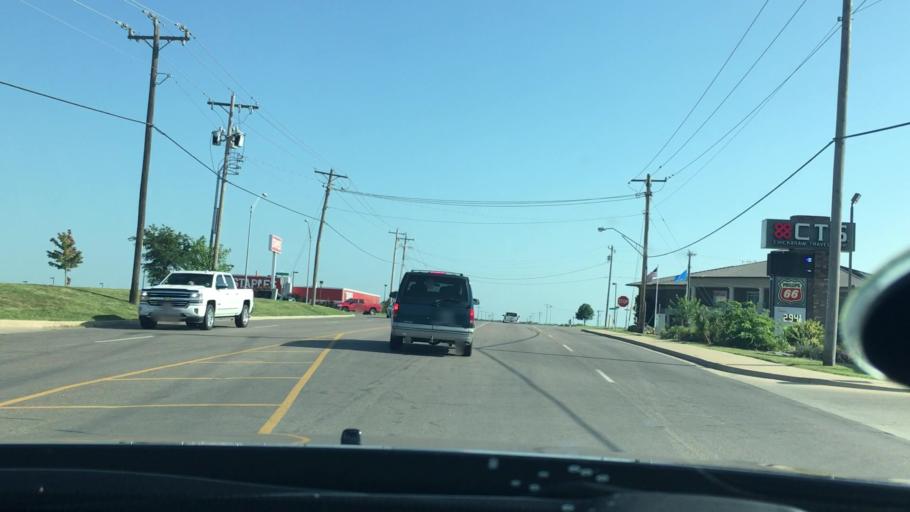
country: US
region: Oklahoma
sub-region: Pontotoc County
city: Ada
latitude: 34.7896
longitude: -96.6523
